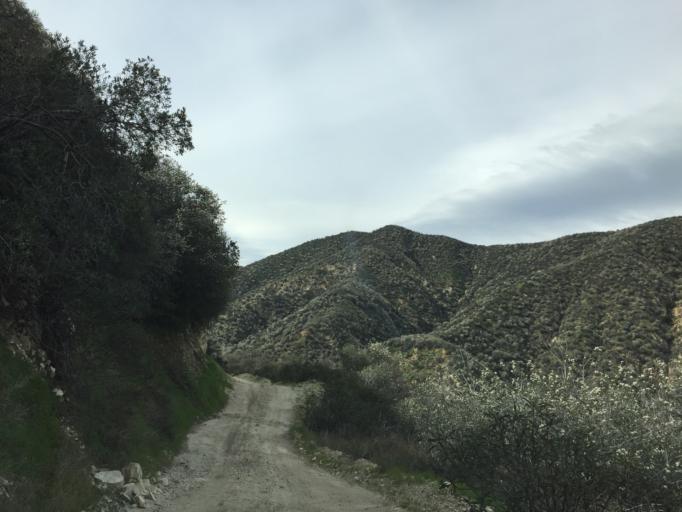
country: US
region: California
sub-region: San Bernardino County
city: Mentone
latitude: 34.1192
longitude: -117.0621
